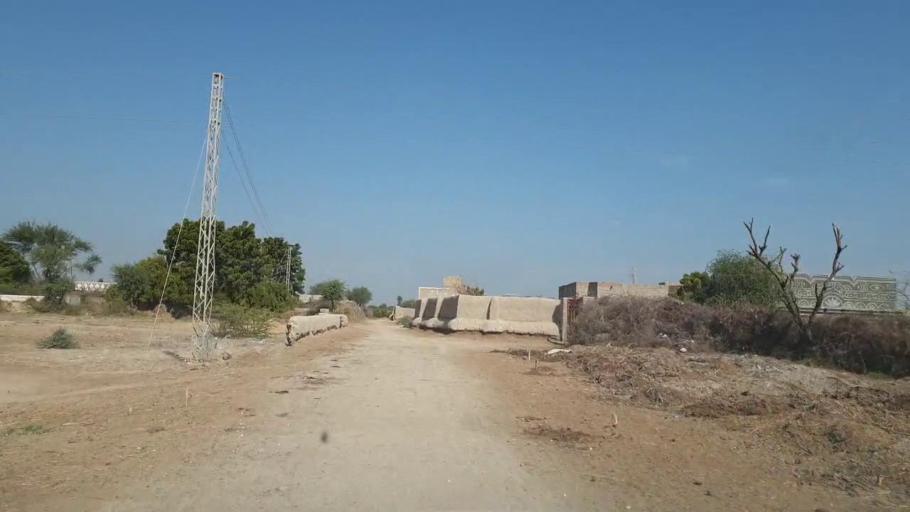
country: PK
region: Sindh
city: Mirpur Khas
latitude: 25.6294
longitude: 69.0955
